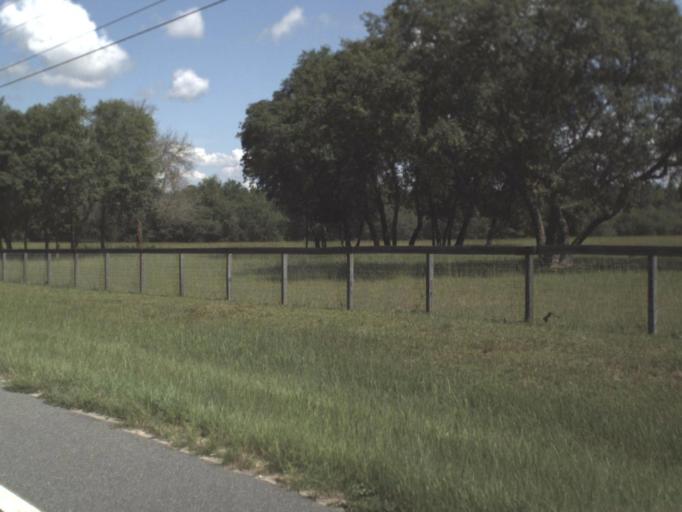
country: US
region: Florida
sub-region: Clay County
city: Keystone Heights
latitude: 29.7435
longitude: -81.9763
